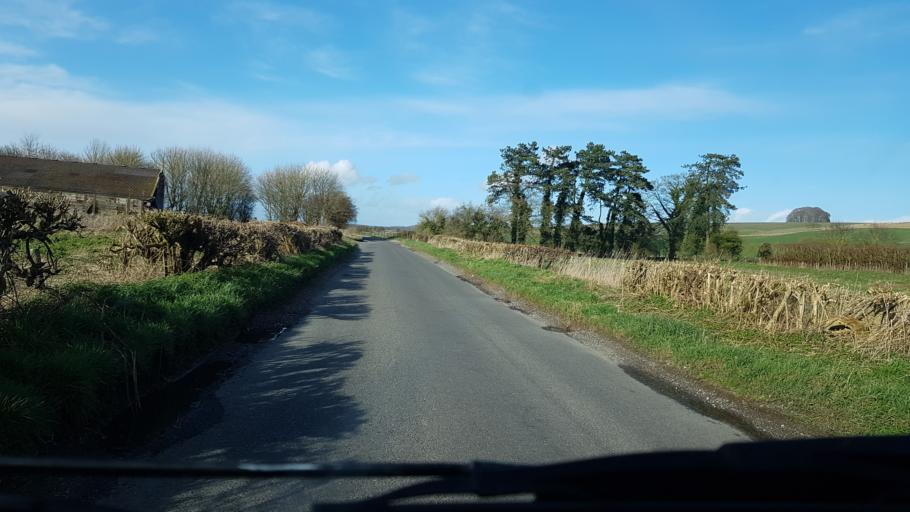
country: GB
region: England
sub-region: Wiltshire
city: Avebury
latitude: 51.4144
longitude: -1.8408
